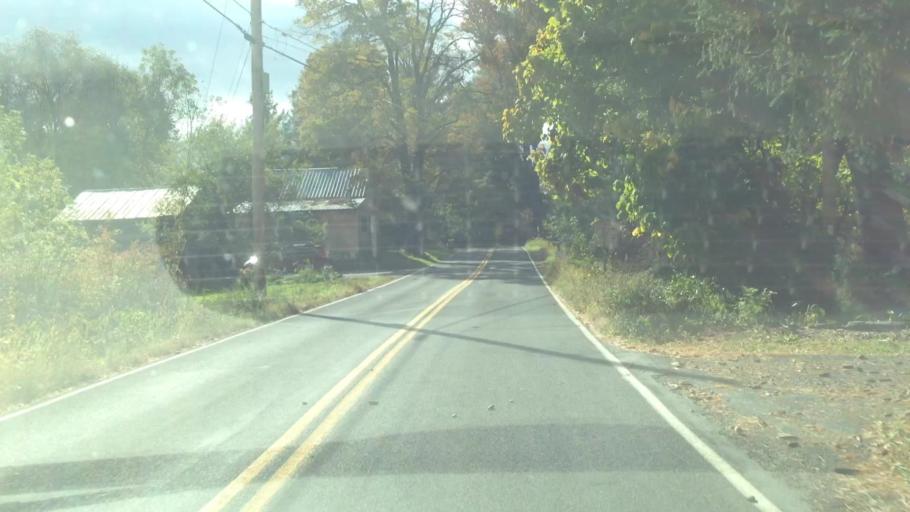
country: US
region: New York
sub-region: Ulster County
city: Tillson
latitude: 41.7996
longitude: -74.0868
